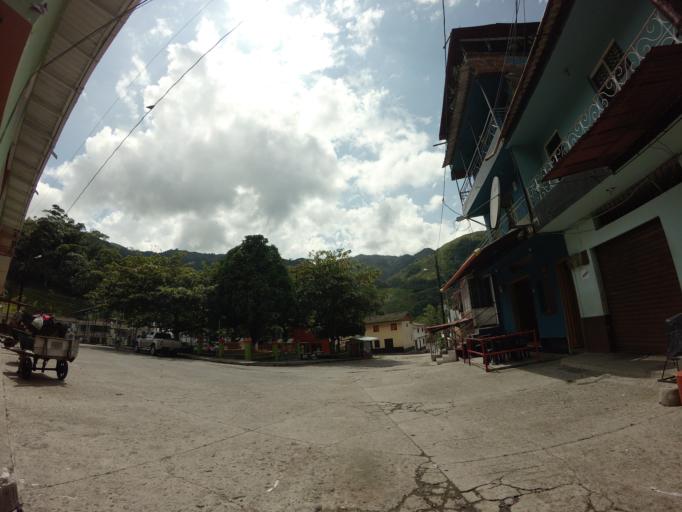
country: CO
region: Antioquia
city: Narino
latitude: 5.5209
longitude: -75.1934
